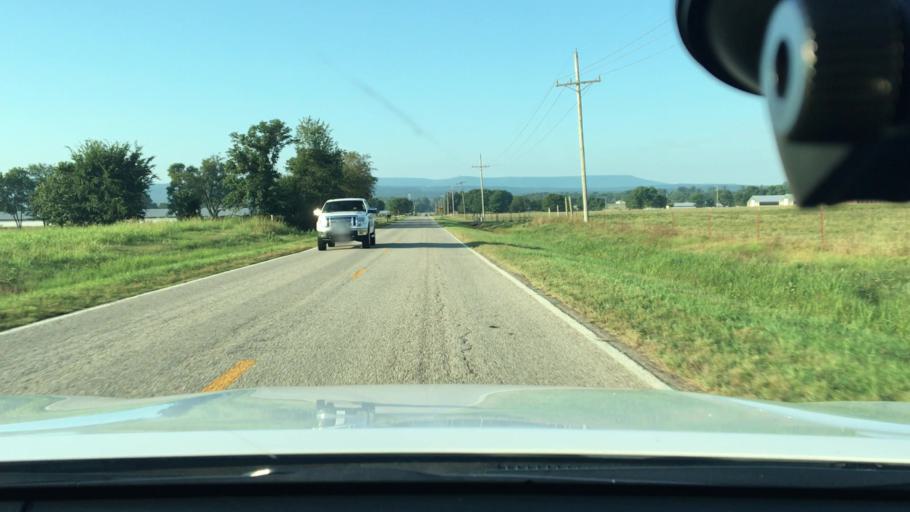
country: US
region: Arkansas
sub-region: Logan County
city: Paris
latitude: 35.3321
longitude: -93.6320
